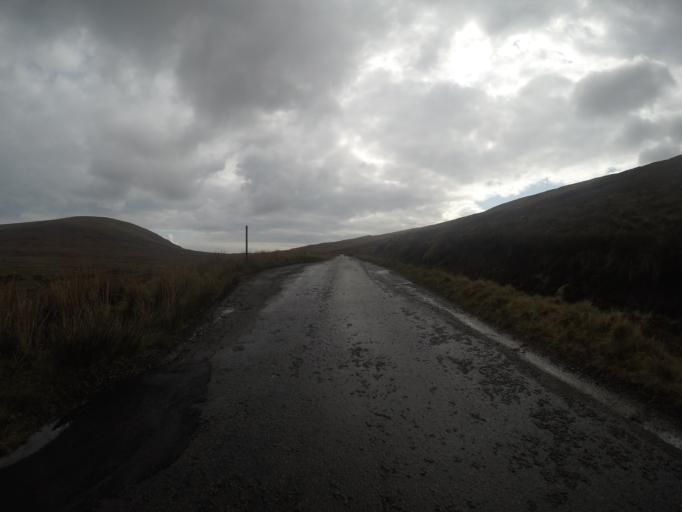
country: GB
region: Scotland
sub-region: Highland
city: Portree
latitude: 57.6225
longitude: -6.3180
